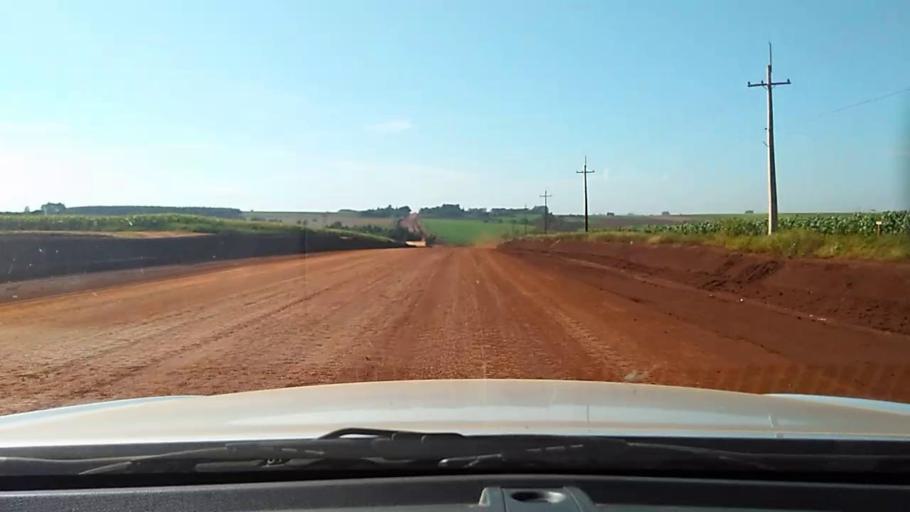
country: PY
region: Alto Parana
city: Naranjal
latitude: -25.9221
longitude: -55.4117
